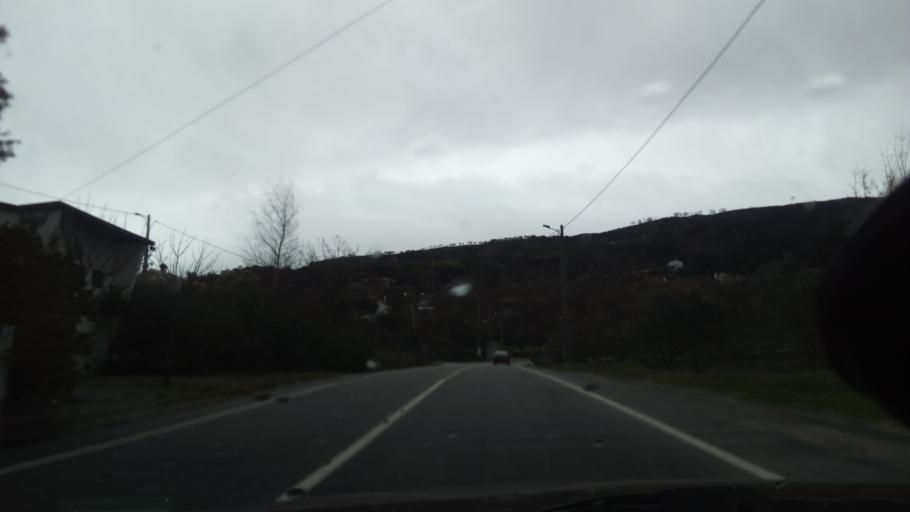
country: PT
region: Guarda
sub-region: Manteigas
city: Manteigas
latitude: 40.5049
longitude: -7.5851
